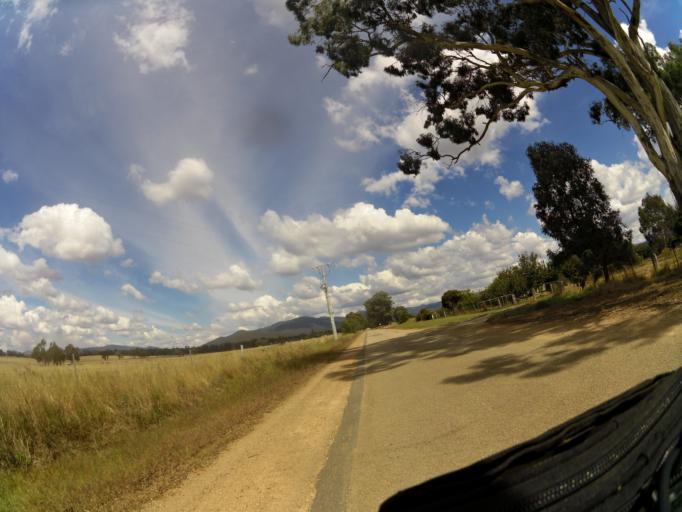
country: AU
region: Victoria
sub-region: Benalla
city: Benalla
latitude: -36.7553
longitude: 145.9784
